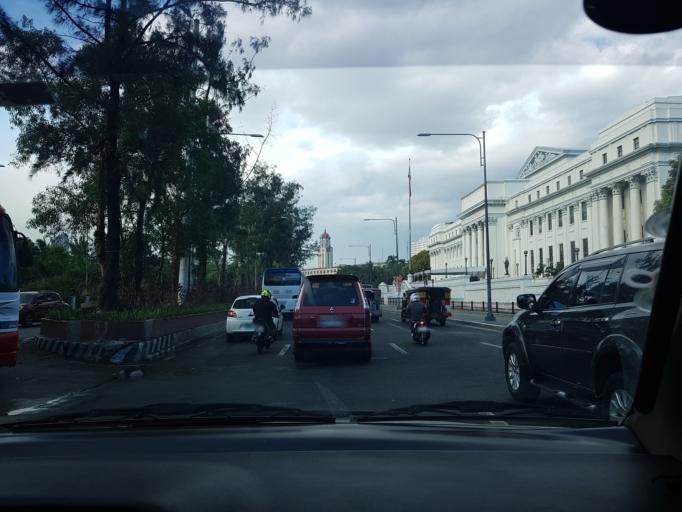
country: PH
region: Metro Manila
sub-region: City of Manila
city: Port Area
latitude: 14.5861
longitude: 120.9804
